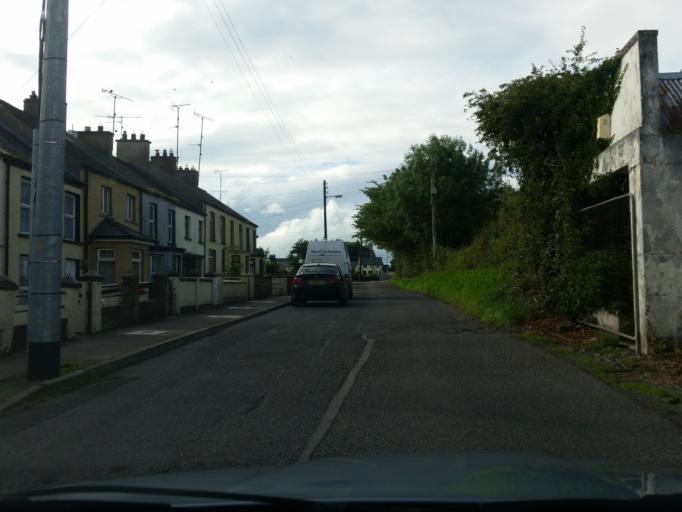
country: IE
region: Ulster
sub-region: County Monaghan
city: Clones
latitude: 54.1881
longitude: -7.2369
